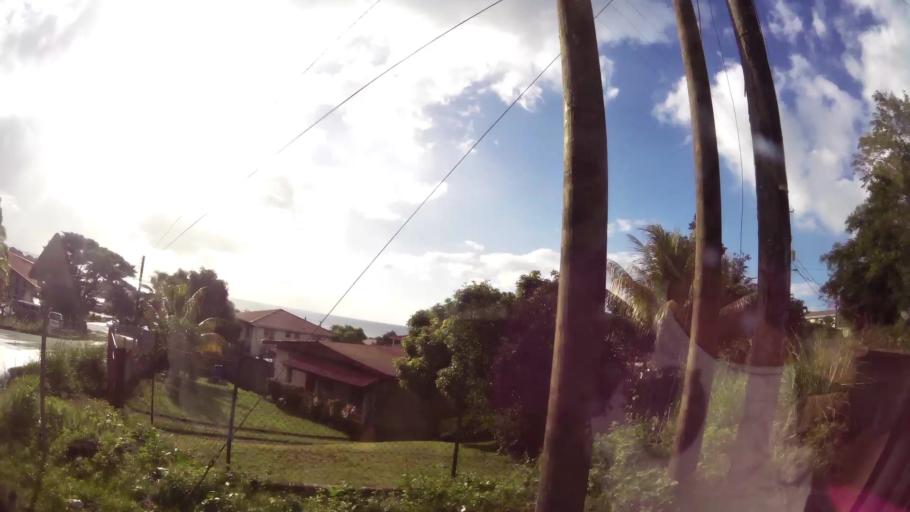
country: DM
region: Saint Paul
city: Mahaut
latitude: 15.3366
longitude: -61.3888
